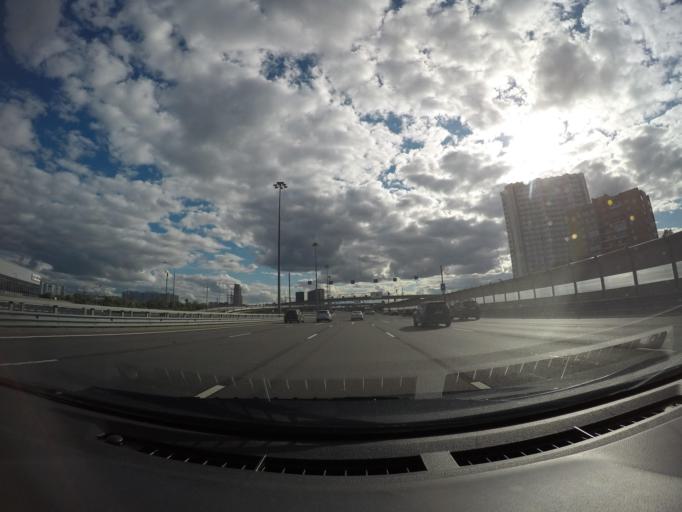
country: RU
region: Moskovskaya
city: Levoberezhnaya
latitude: 55.8901
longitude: 37.4843
